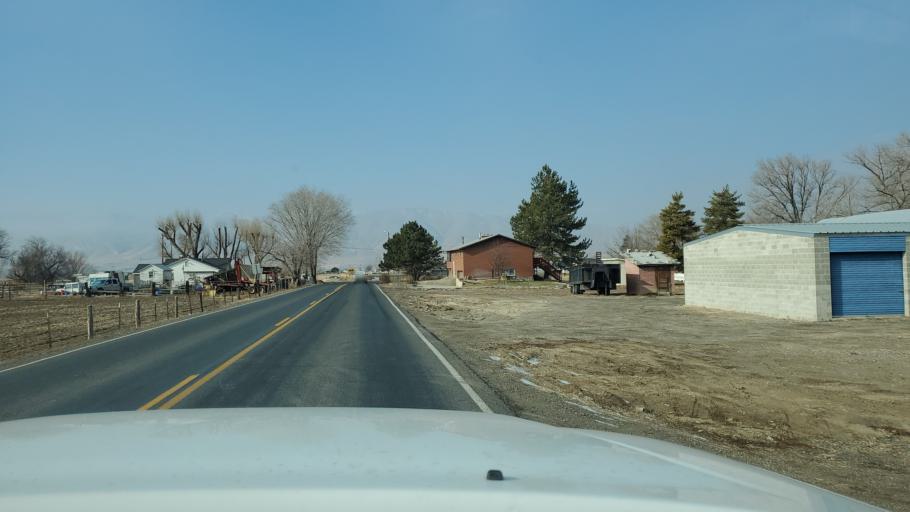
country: US
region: Utah
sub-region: Utah County
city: Benjamin
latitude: 40.0853
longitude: -111.7294
